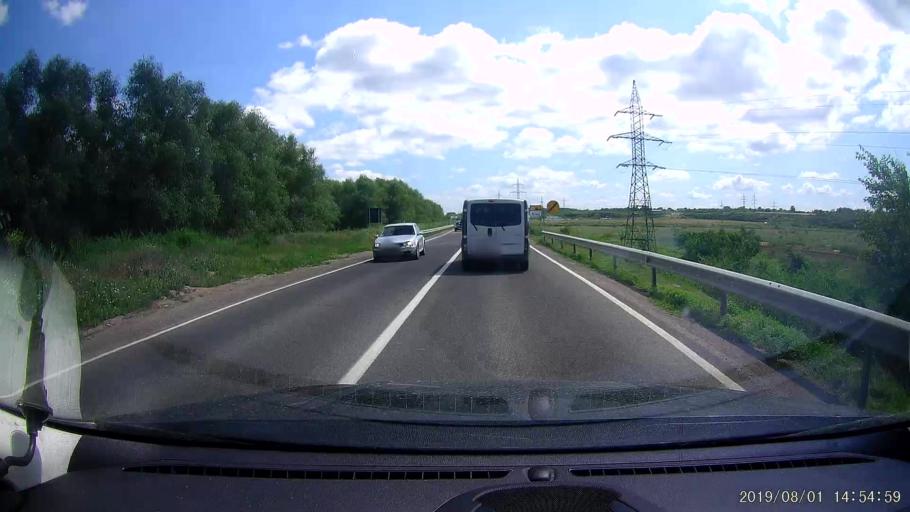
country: RO
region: Braila
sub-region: Municipiul Braila
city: Braila
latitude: 45.3104
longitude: 27.9829
